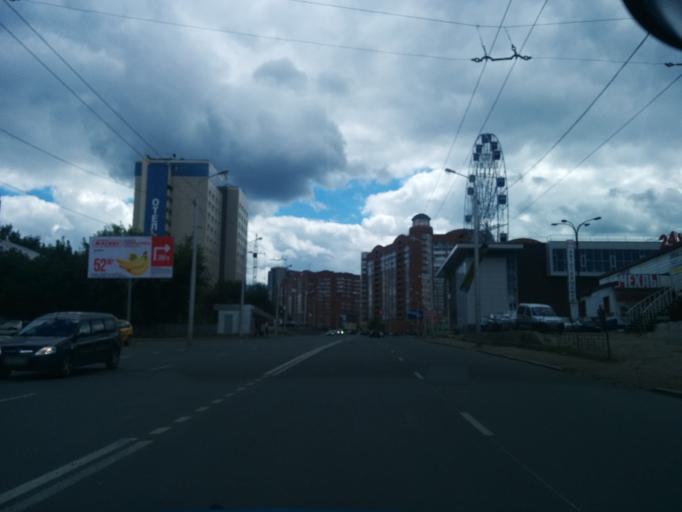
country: RU
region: Bashkortostan
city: Ufa
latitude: 54.7155
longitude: 55.9946
